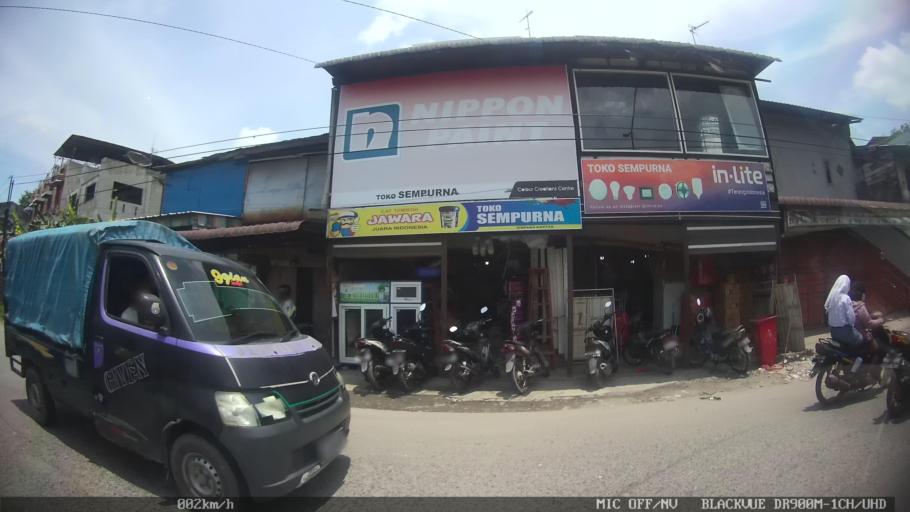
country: ID
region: North Sumatra
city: Labuhan Deli
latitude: 3.7237
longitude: 98.6790
